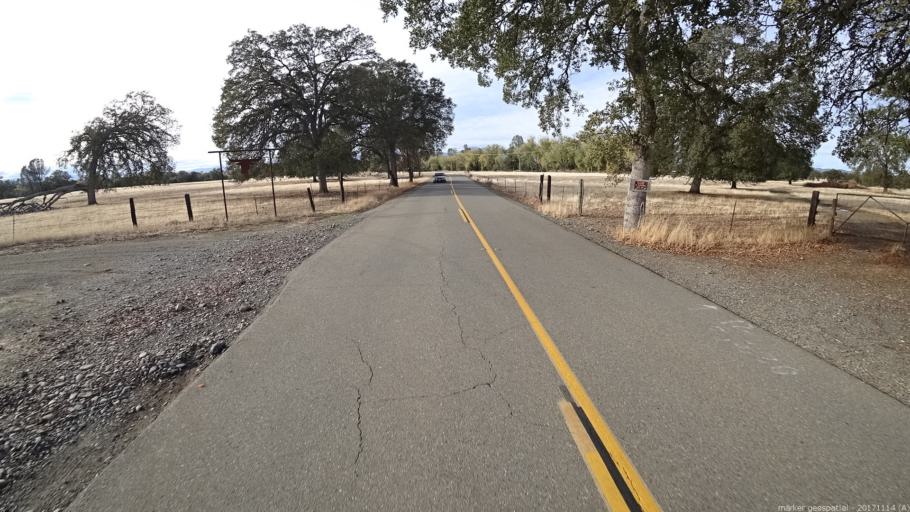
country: US
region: California
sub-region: Shasta County
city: Shasta
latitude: 40.3912
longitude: -122.5012
